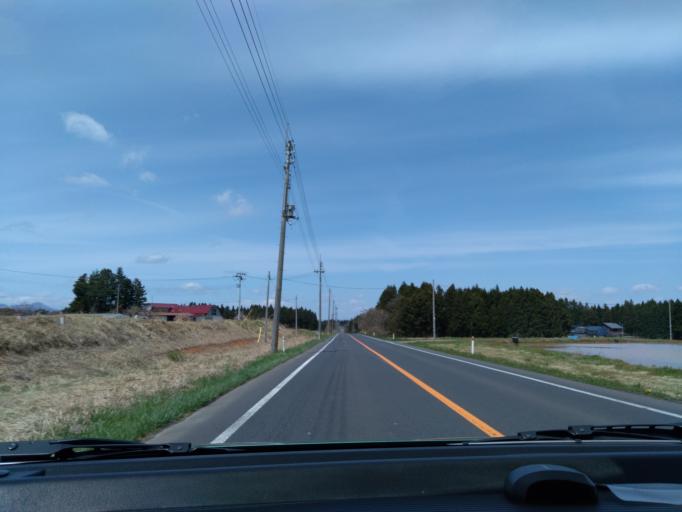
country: JP
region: Iwate
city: Mizusawa
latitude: 39.0896
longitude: 141.0514
